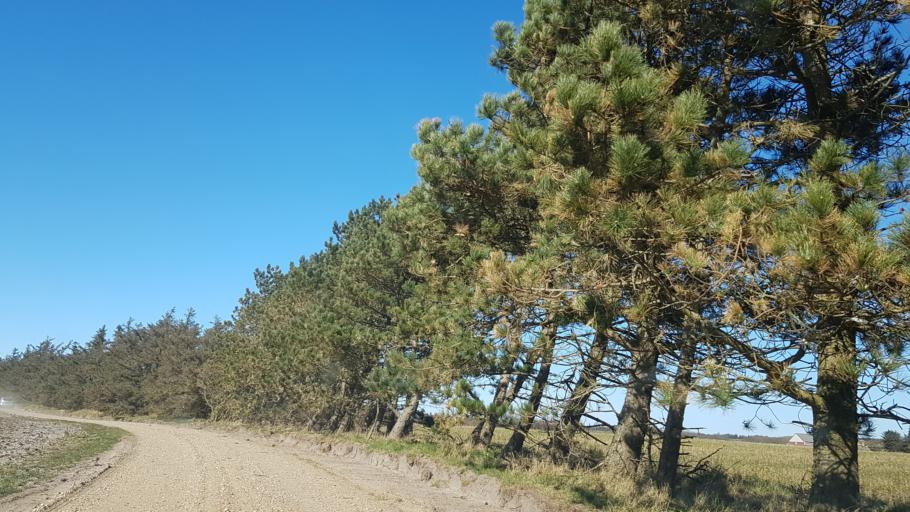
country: DK
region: South Denmark
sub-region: Esbjerg Kommune
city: Ribe
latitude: 55.2448
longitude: 8.7134
